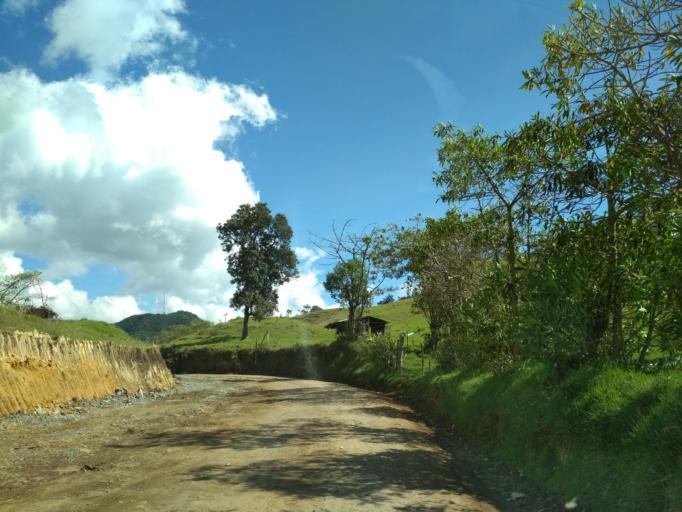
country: CO
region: Cauca
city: Jambalo
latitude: 2.7044
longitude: -76.3279
